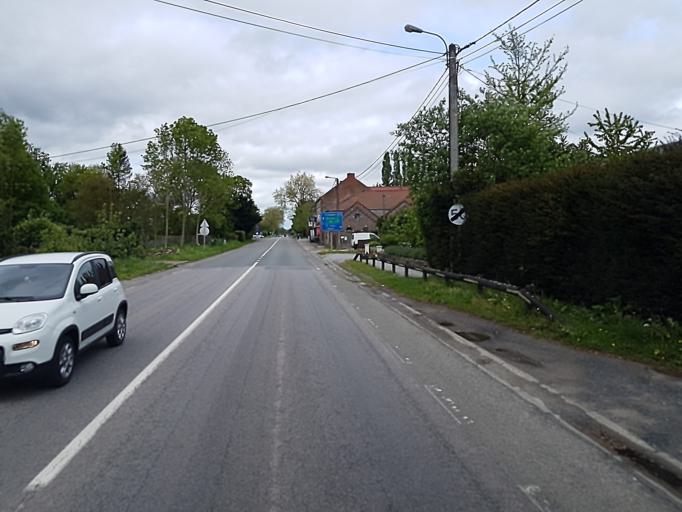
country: BE
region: Wallonia
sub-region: Province du Brabant Wallon
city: Jodoigne
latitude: 50.7357
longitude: 4.8814
